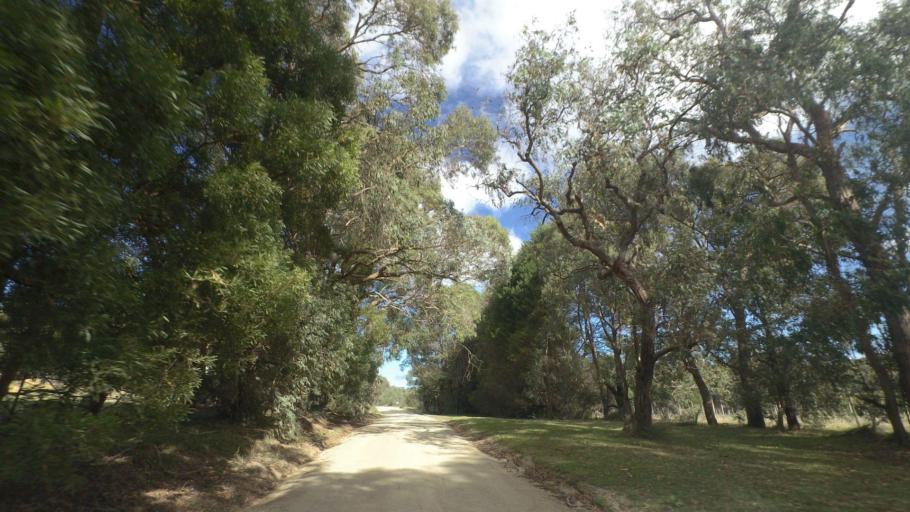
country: AU
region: Victoria
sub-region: Cardinia
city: Gembrook
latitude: -37.9854
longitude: 145.6107
